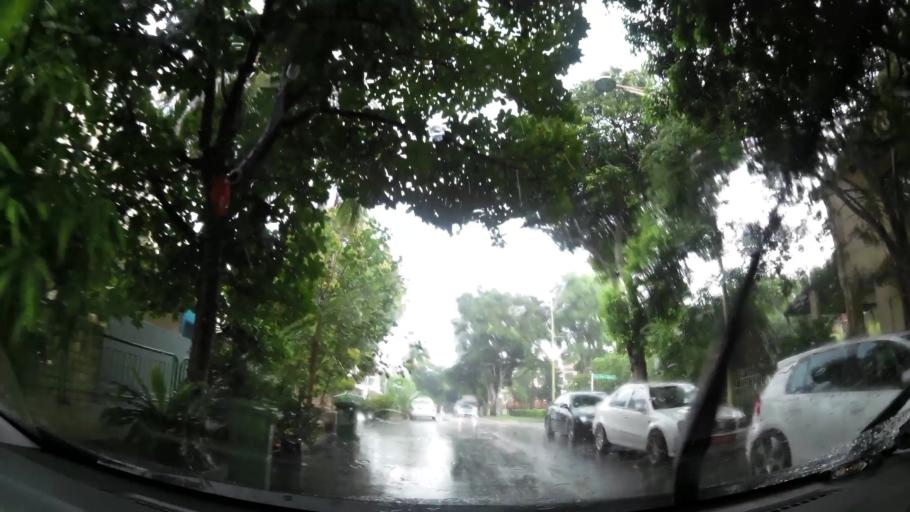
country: SG
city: Singapore
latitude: 1.3330
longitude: 103.9433
